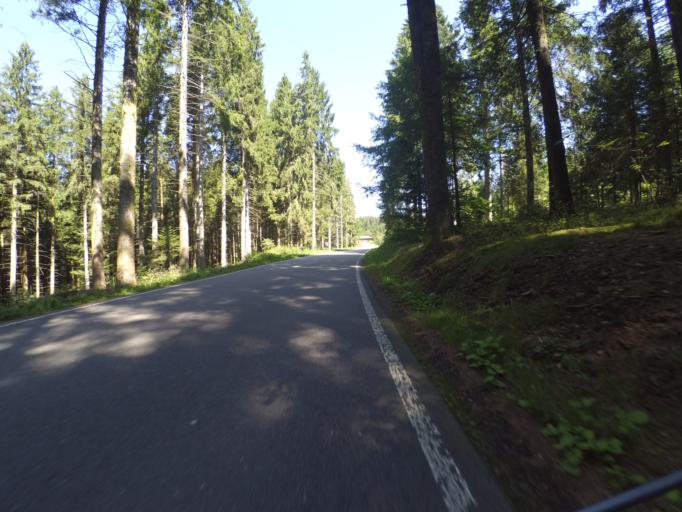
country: DE
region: Baden-Wuerttemberg
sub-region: Freiburg Region
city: Gutenbach
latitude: 48.0350
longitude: 8.1752
